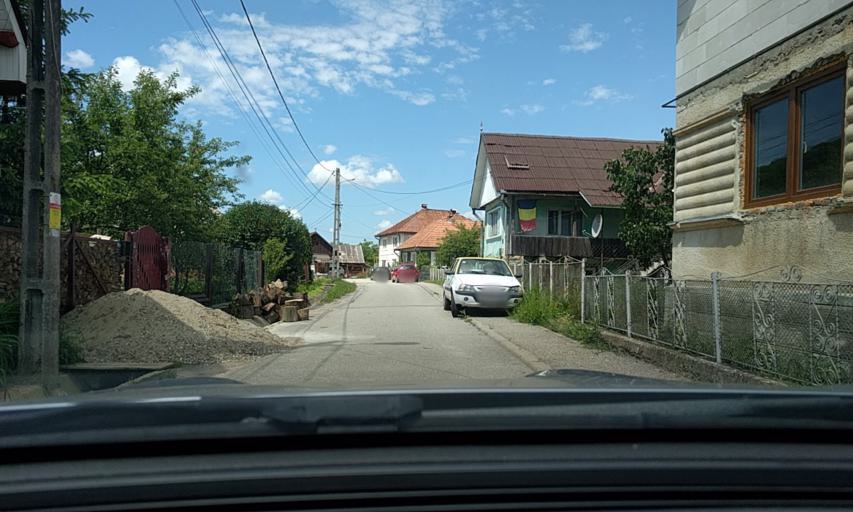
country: RO
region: Bistrita-Nasaud
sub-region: Oras Nasaud
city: Nasaud
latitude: 47.2793
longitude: 24.4041
